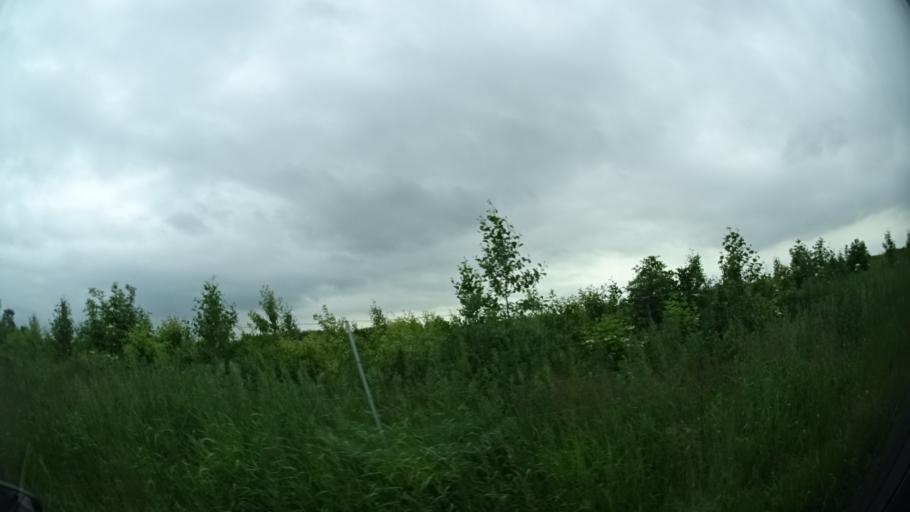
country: DK
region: Central Jutland
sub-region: Arhus Kommune
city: Solbjerg
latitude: 56.0557
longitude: 10.1088
